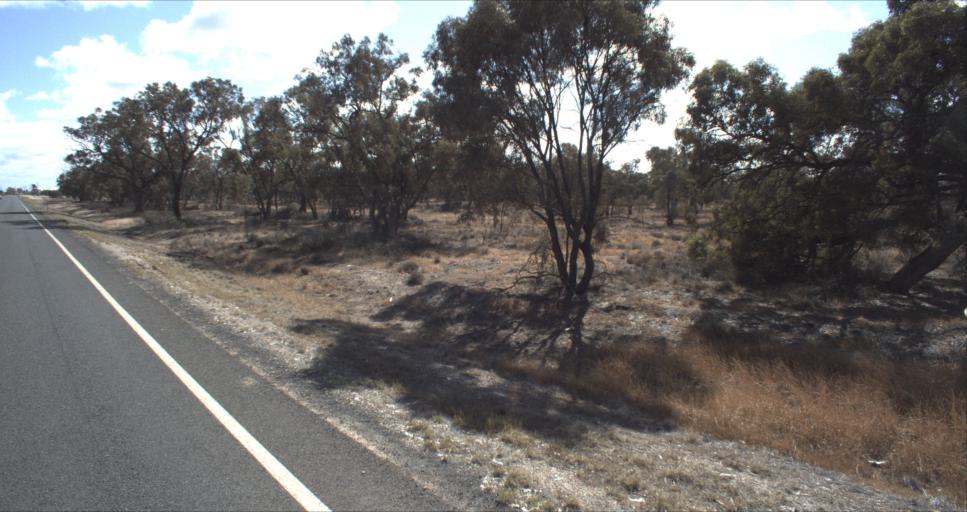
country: AU
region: New South Wales
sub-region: Murrumbidgee Shire
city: Darlington Point
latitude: -34.5232
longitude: 146.1753
